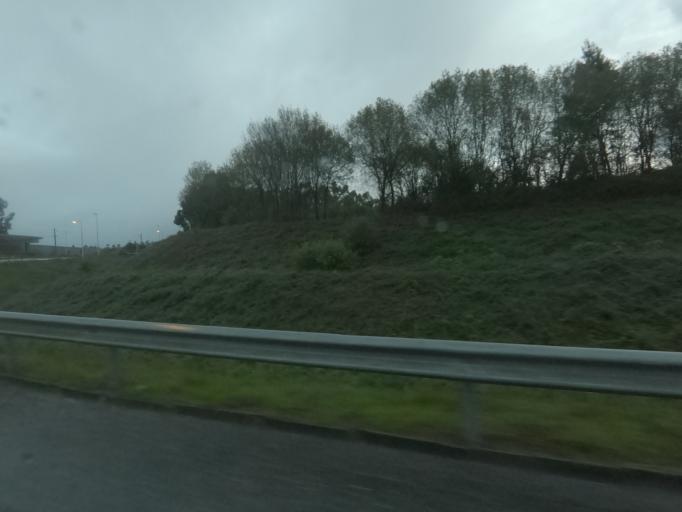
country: PT
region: Braga
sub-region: Braga
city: Oliveira
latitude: 41.5366
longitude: -8.4972
